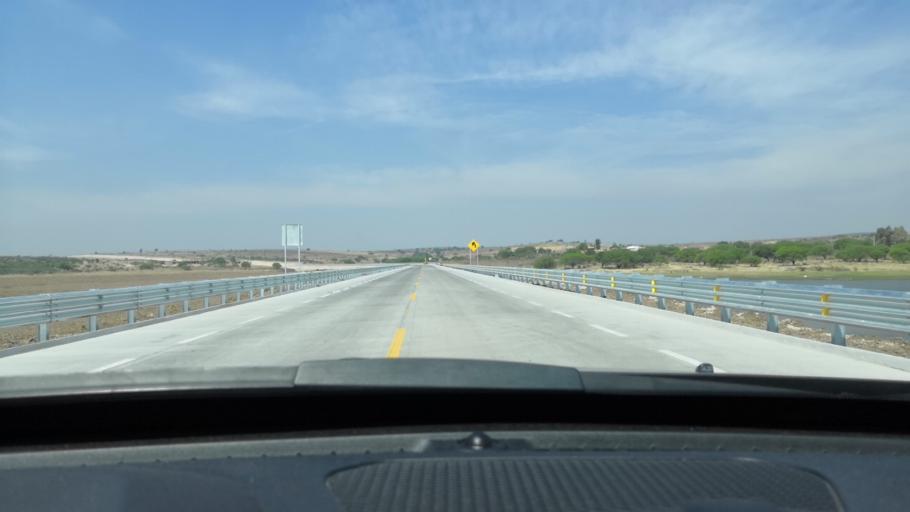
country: MX
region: Guanajuato
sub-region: Purisima del Rincon
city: Potrerillos (Guanajal)
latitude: 21.0853
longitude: -101.8459
